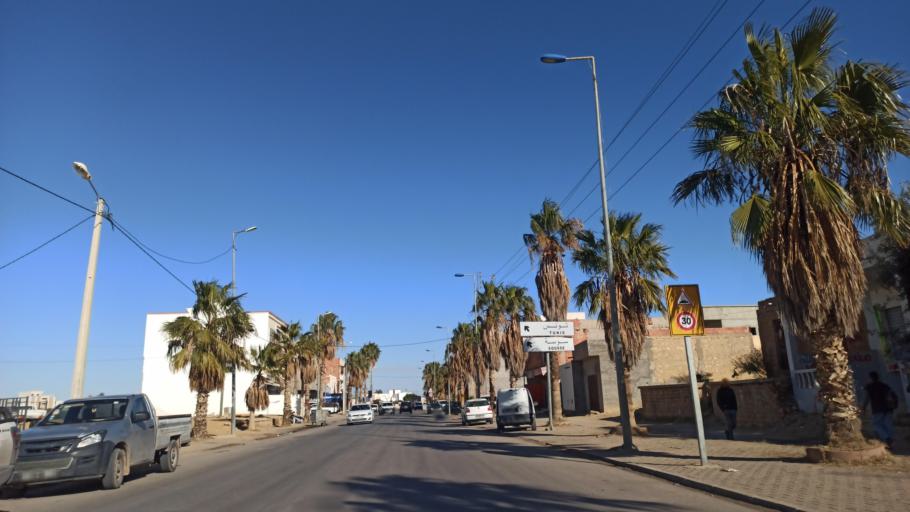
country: TN
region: Sidi Bu Zayd
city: Jilma
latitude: 35.2682
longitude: 9.4163
